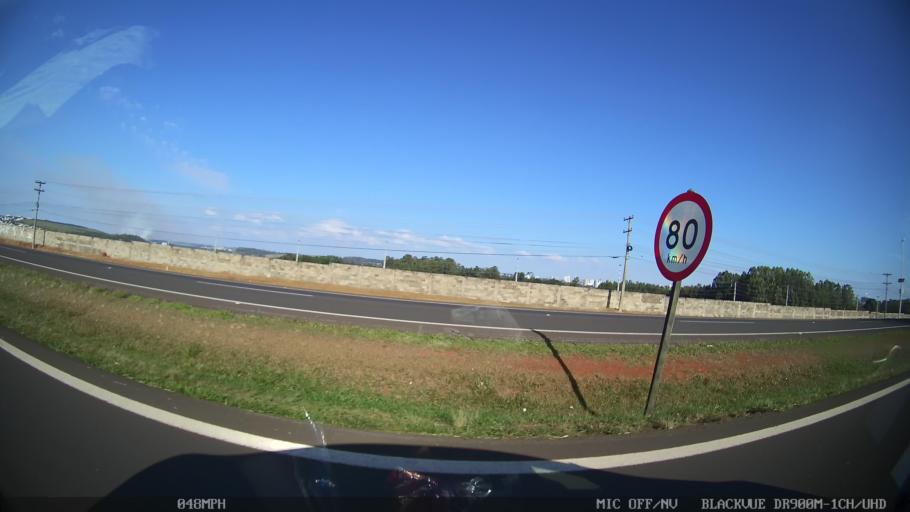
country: BR
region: Sao Paulo
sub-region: Piracicaba
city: Piracicaba
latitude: -22.6893
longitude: -47.6429
